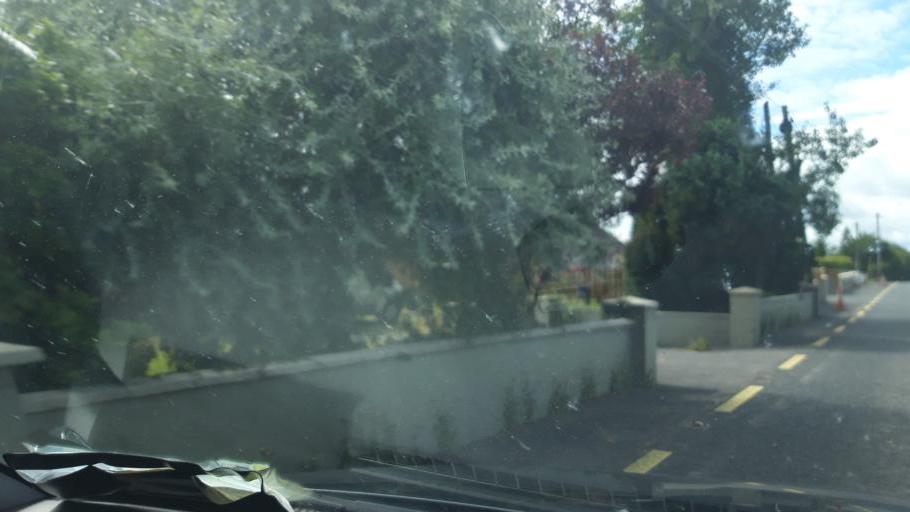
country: IE
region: Leinster
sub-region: Kilkenny
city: Callan
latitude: 52.5260
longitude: -7.4154
